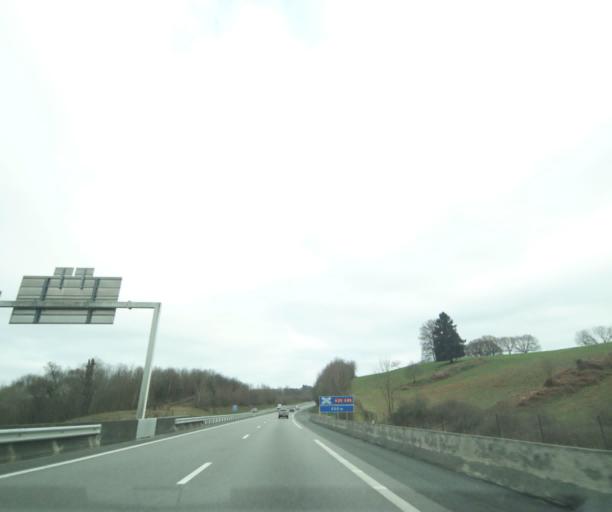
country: FR
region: Limousin
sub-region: Departement de la Correze
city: Saint-Mexant
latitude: 45.3130
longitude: 1.5753
